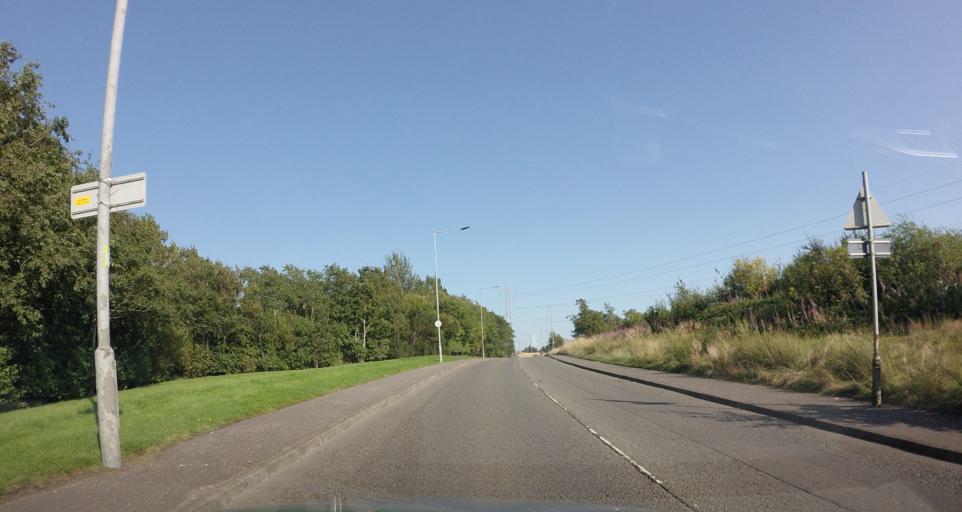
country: GB
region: Scotland
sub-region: South Lanarkshire
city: East Kilbride
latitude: 55.7417
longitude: -4.1893
